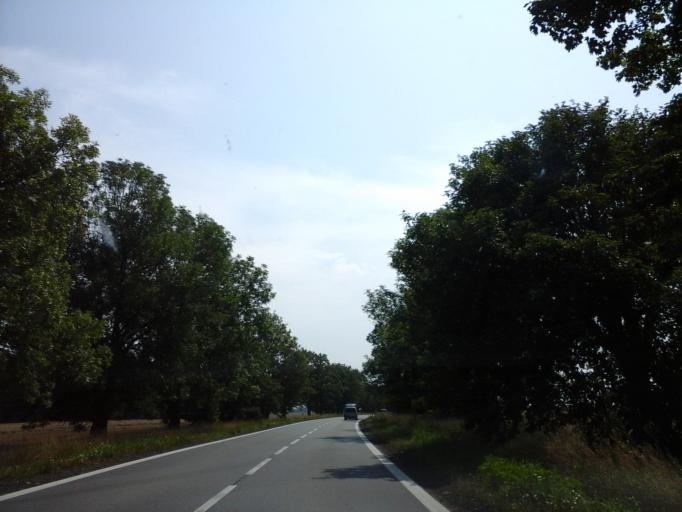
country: PL
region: Lower Silesian Voivodeship
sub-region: Powiat wroclawski
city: Zerniki Wroclawskie
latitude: 51.0168
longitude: 17.0638
